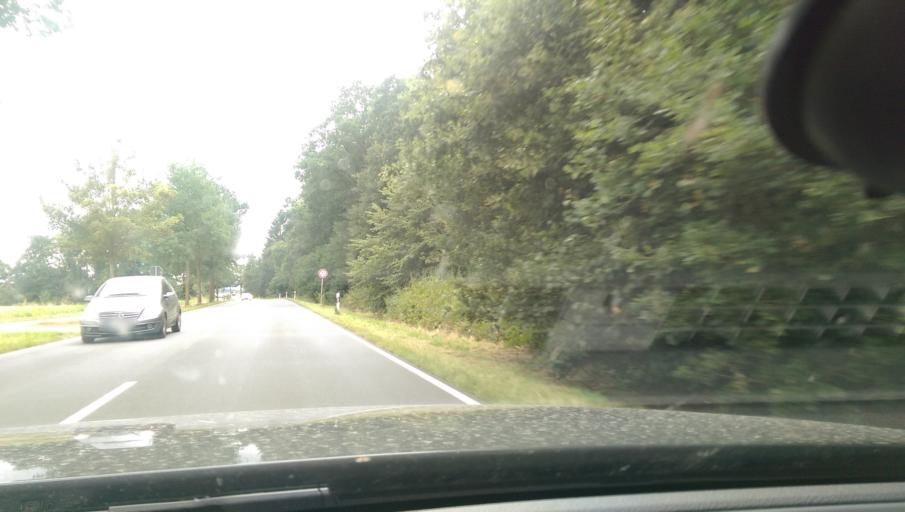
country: DE
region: Lower Saxony
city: Neustadt am Rubenberge
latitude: 52.5453
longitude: 9.4751
